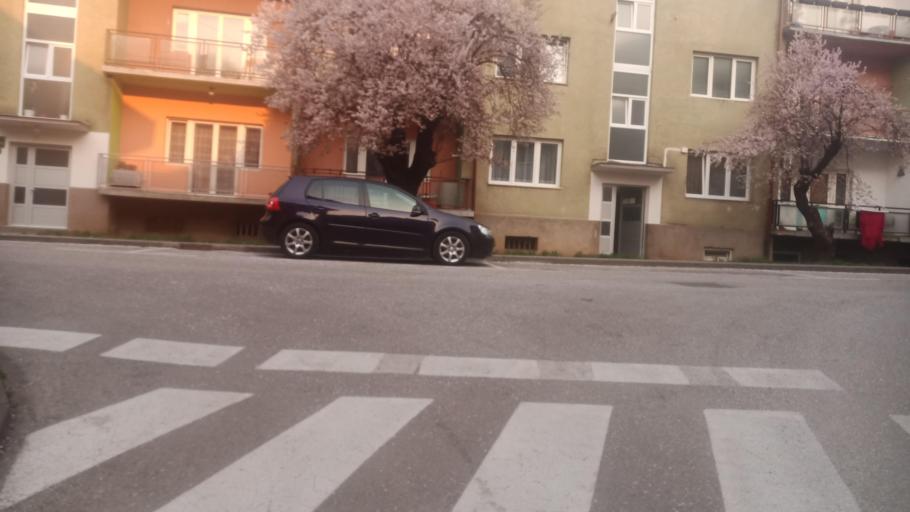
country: BA
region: Federation of Bosnia and Herzegovina
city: Bosanska Krupa
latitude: 44.8840
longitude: 16.1559
